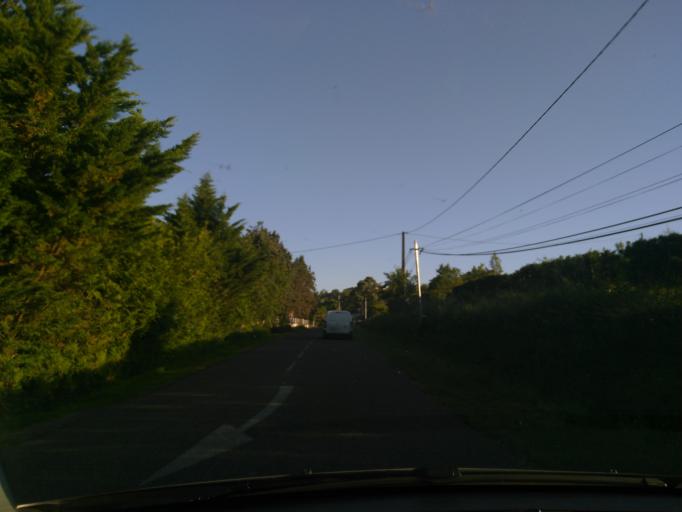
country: FR
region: Midi-Pyrenees
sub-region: Departement du Gers
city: Valence-sur-Baise
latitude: 43.8727
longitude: 0.4669
